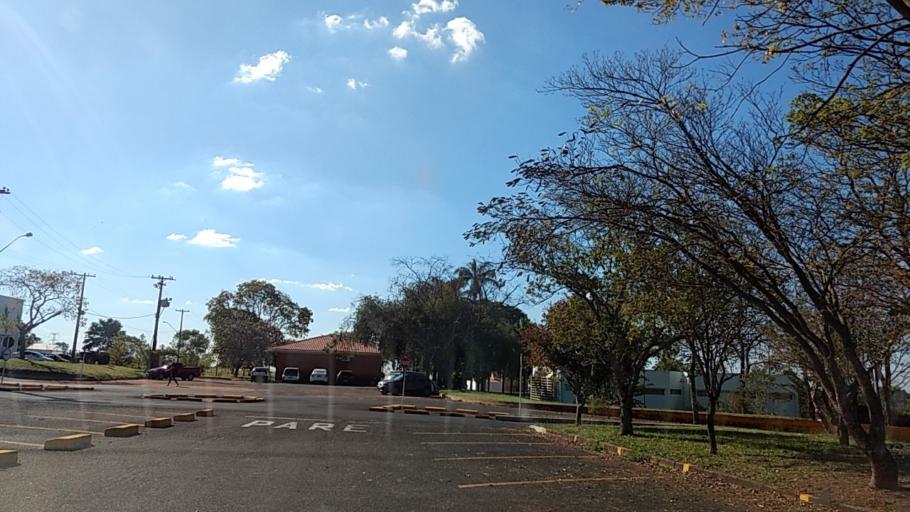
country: BR
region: Sao Paulo
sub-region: Botucatu
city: Botucatu
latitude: -22.8495
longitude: -48.4347
